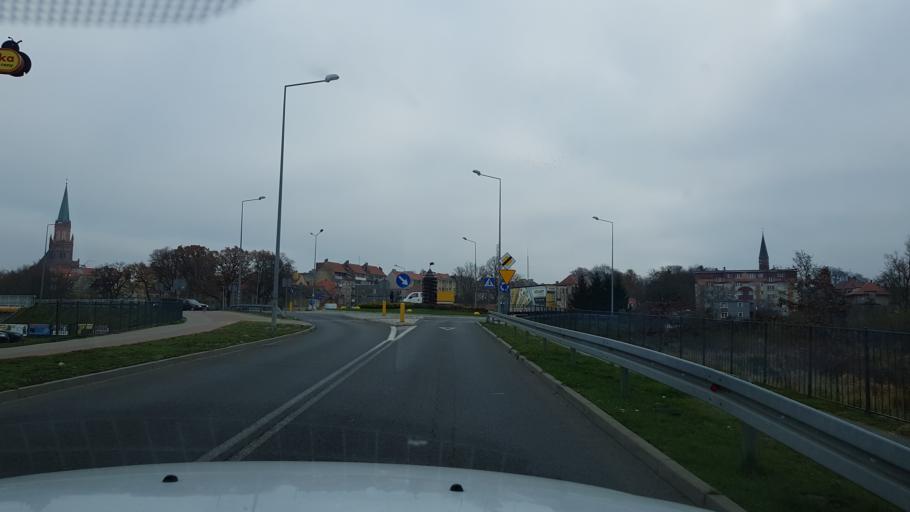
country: PL
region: West Pomeranian Voivodeship
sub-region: Powiat gryficki
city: Trzebiatow
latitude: 54.0635
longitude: 15.2585
